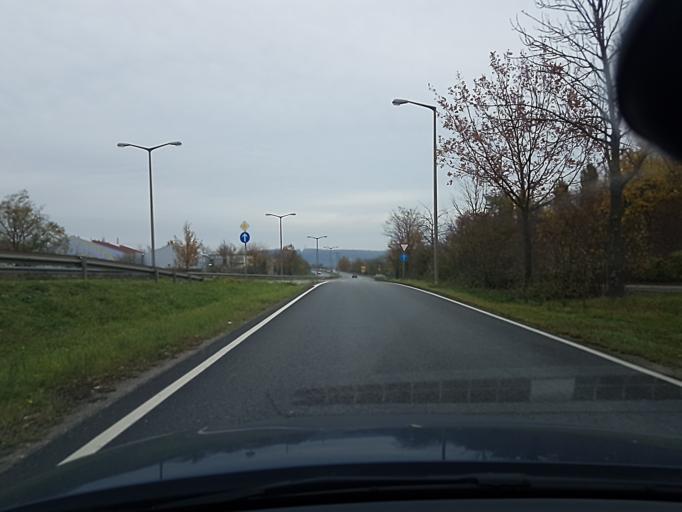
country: DE
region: Bavaria
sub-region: Upper Palatinate
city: Regensburg
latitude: 49.0076
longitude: 12.1382
